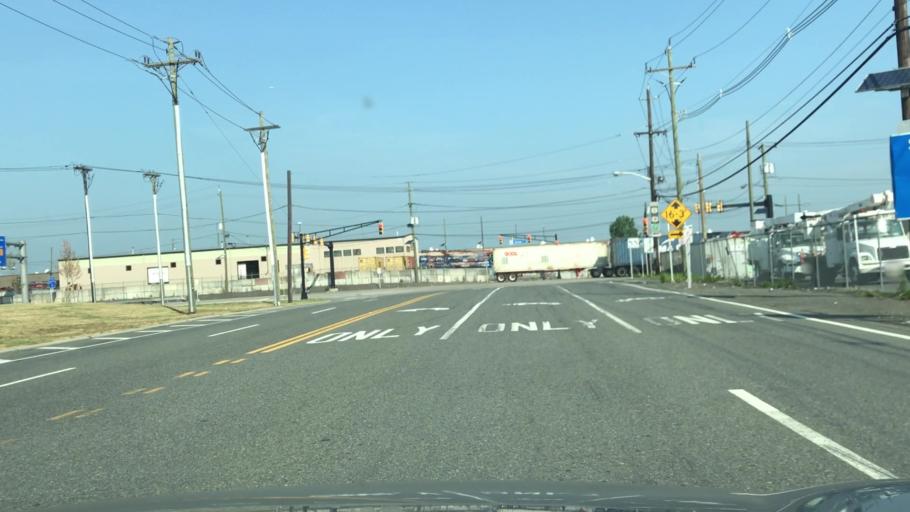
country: US
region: New Jersey
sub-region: Hudson County
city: Bayonne
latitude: 40.6737
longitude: -74.1591
